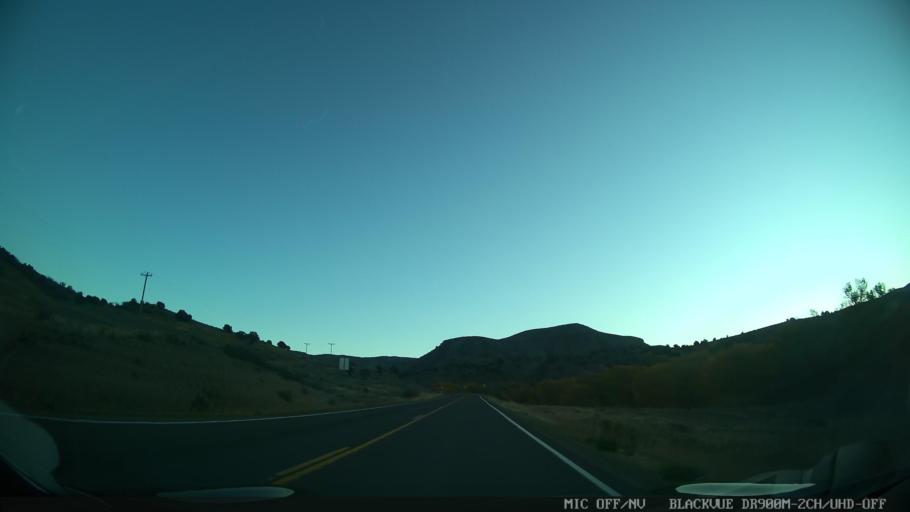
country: US
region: Colorado
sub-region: Eagle County
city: Edwards
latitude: 39.7517
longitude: -106.6730
